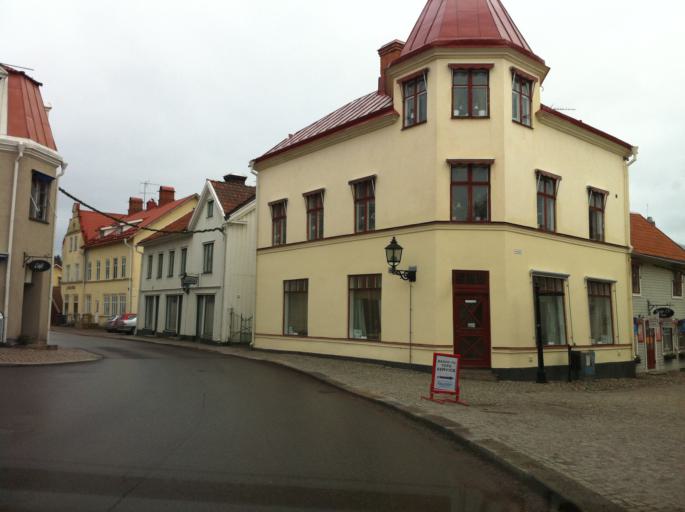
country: SE
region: Kalmar
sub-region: Vasterviks Kommun
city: Overum
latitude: 57.9016
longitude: 16.0517
